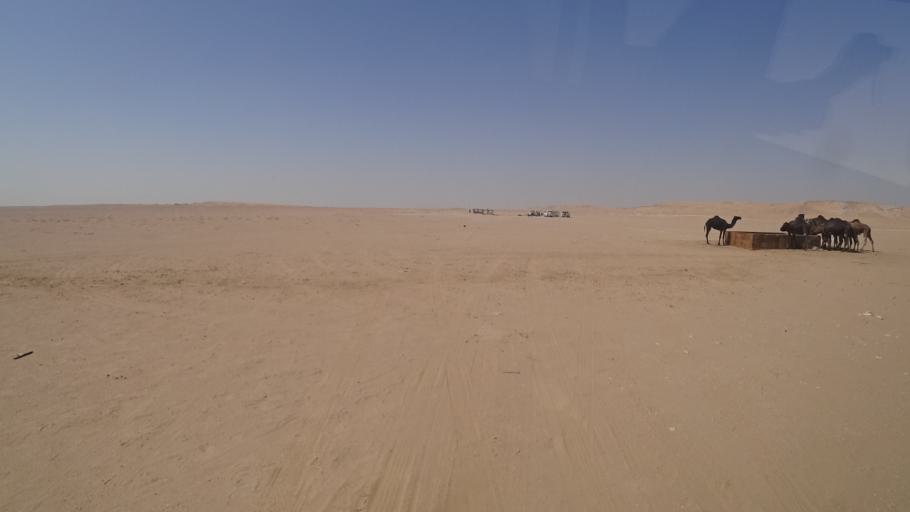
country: YE
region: Al Mahrah
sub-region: Shahan
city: Shihan as Sufla
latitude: 18.5760
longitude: 52.4969
